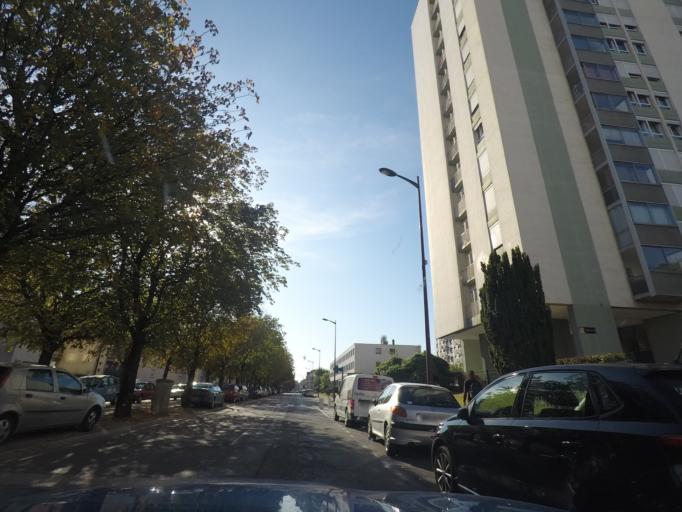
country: FR
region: Lorraine
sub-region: Departement de la Moselle
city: Thionville
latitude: 49.3621
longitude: 6.1561
